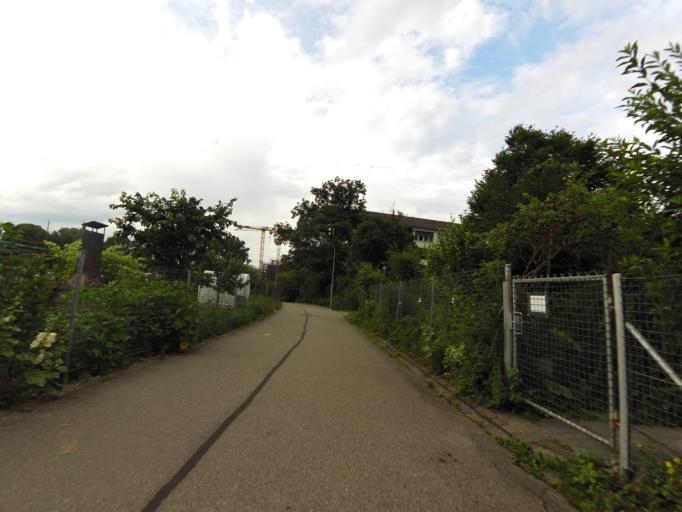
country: CH
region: Zurich
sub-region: Bezirk Zuerich
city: Zuerich (Kreis 9) / Albisrieden
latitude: 47.3781
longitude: 8.4859
